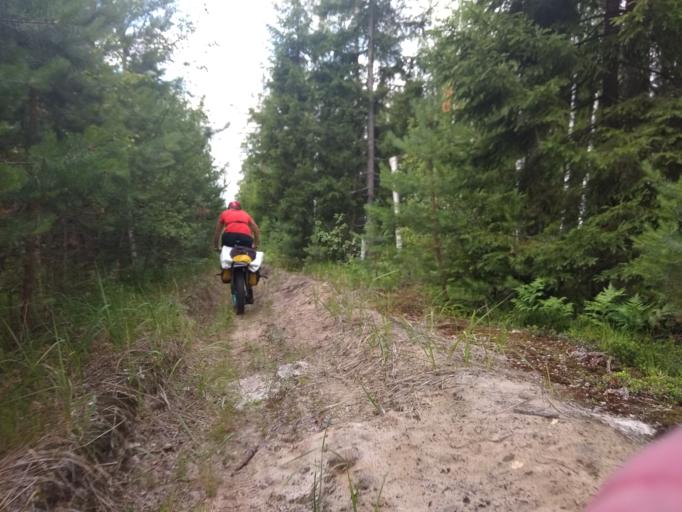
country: RU
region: Moskovskaya
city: Misheronskiy
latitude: 55.6454
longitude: 39.6989
